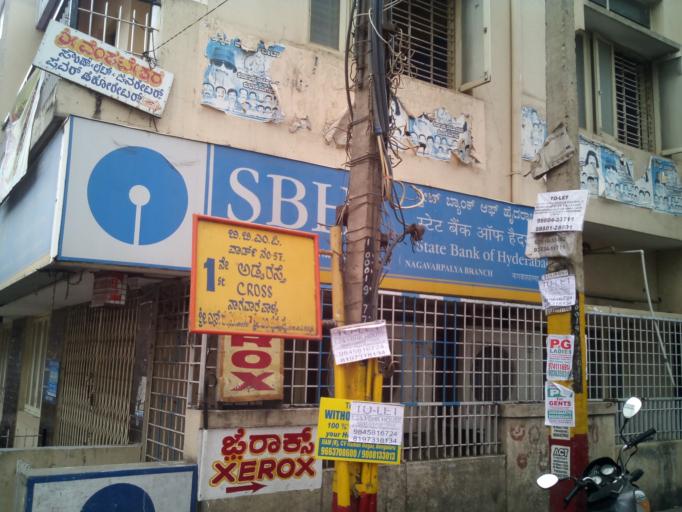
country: IN
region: Karnataka
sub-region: Bangalore Urban
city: Bangalore
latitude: 12.9938
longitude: 77.6637
